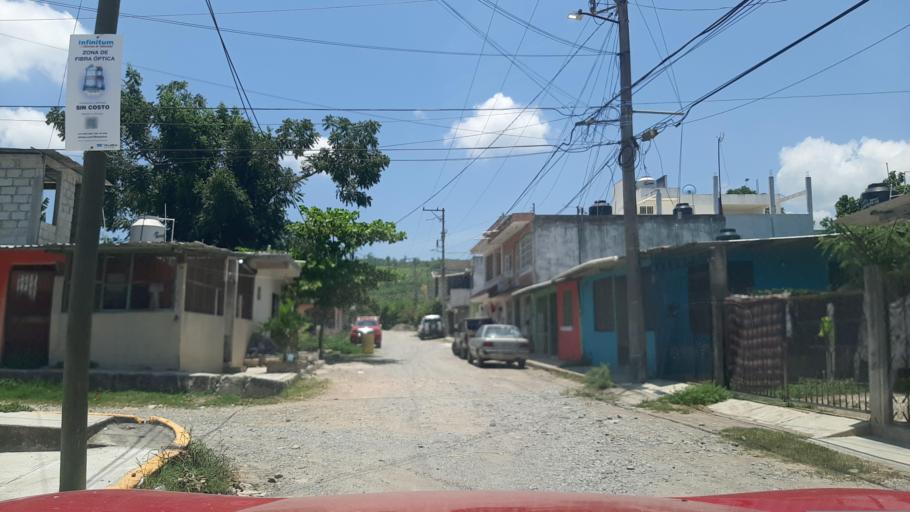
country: MX
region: Veracruz
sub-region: Poza Rica de Hidalgo
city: El Mollejon
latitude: 20.5411
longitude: -97.4103
